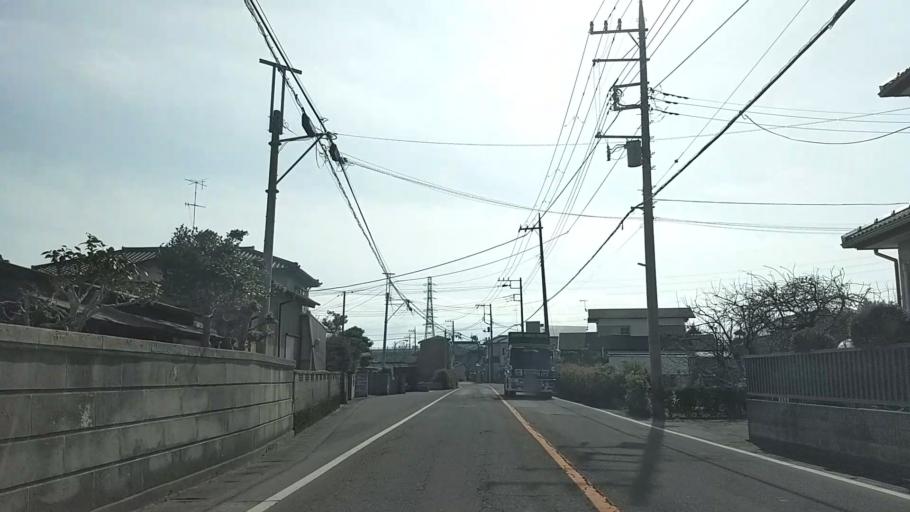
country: JP
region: Kanagawa
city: Chigasaki
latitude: 35.3545
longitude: 139.3848
